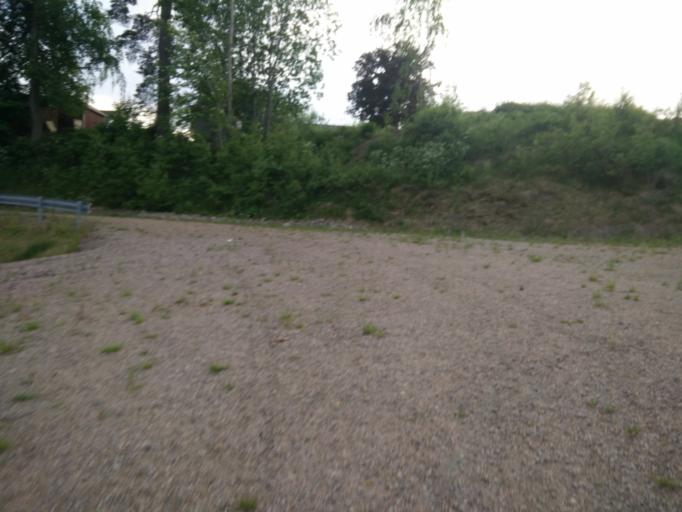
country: SE
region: Vaermland
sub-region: Hagfors Kommun
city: Hagfors
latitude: 60.0002
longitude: 13.5913
